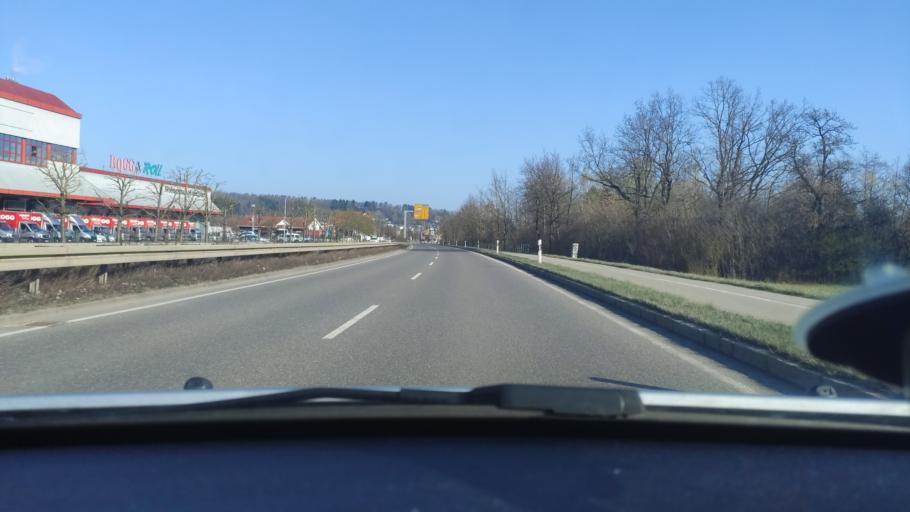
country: DE
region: Baden-Wuerttemberg
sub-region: Tuebingen Region
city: Balingen
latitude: 48.2597
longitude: 8.8547
